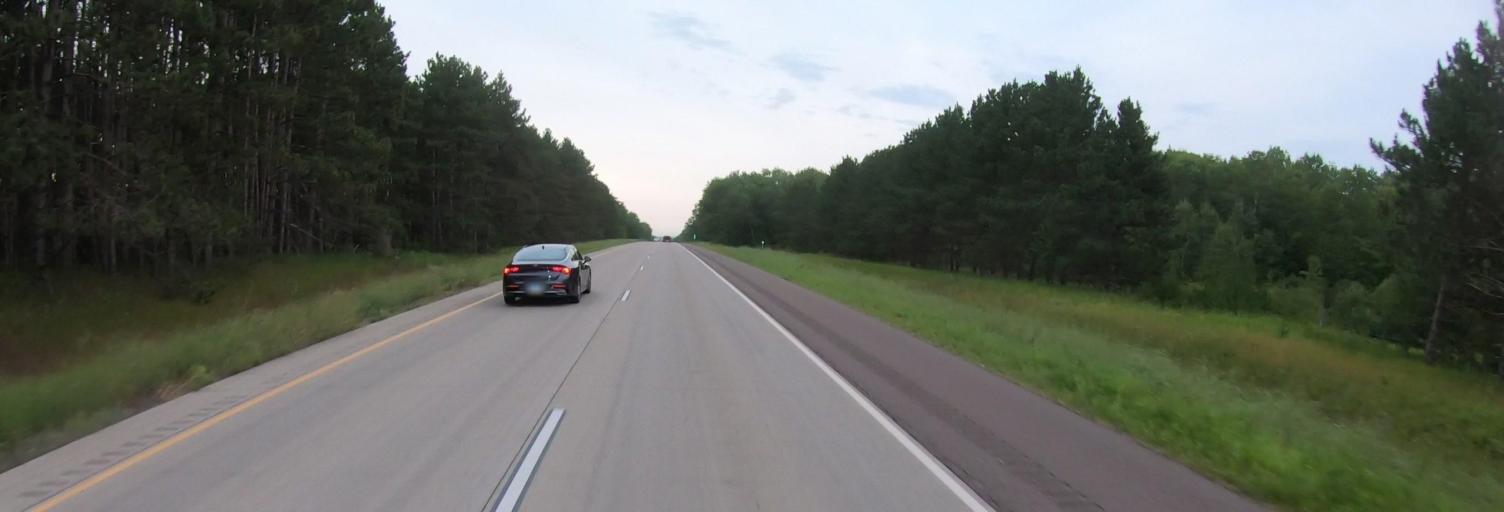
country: US
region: Minnesota
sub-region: Pine County
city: Sandstone
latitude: 46.1970
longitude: -92.8464
